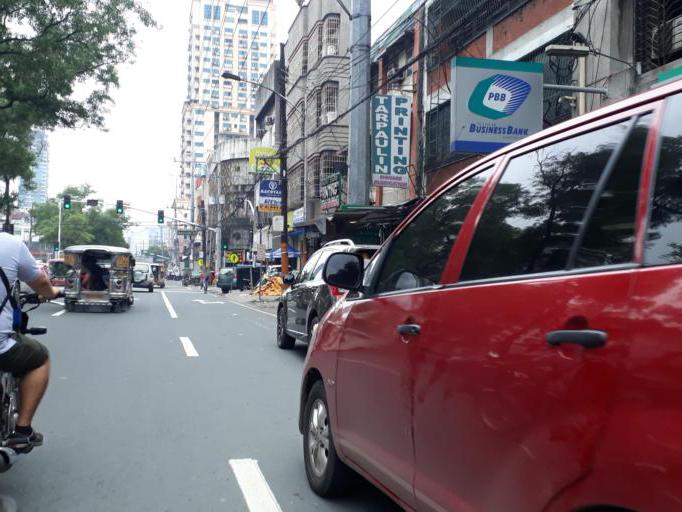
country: PH
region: Metro Manila
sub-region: City of Manila
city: Manila
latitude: 14.6145
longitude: 120.9767
